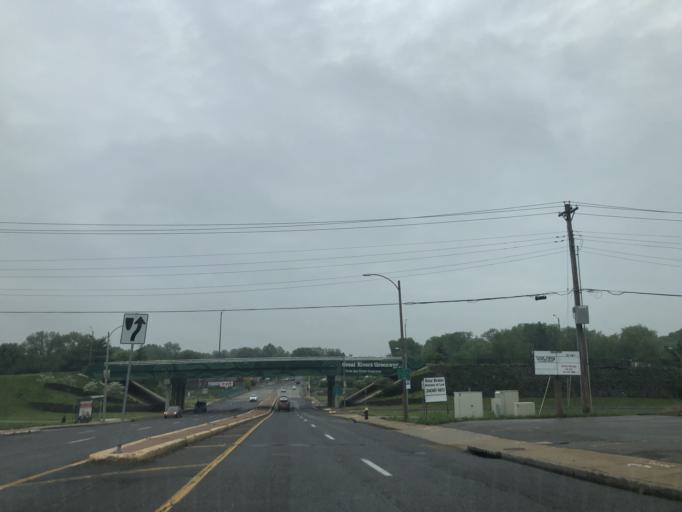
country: US
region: Missouri
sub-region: Saint Louis County
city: Shrewsbury
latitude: 38.5856
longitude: -90.3150
